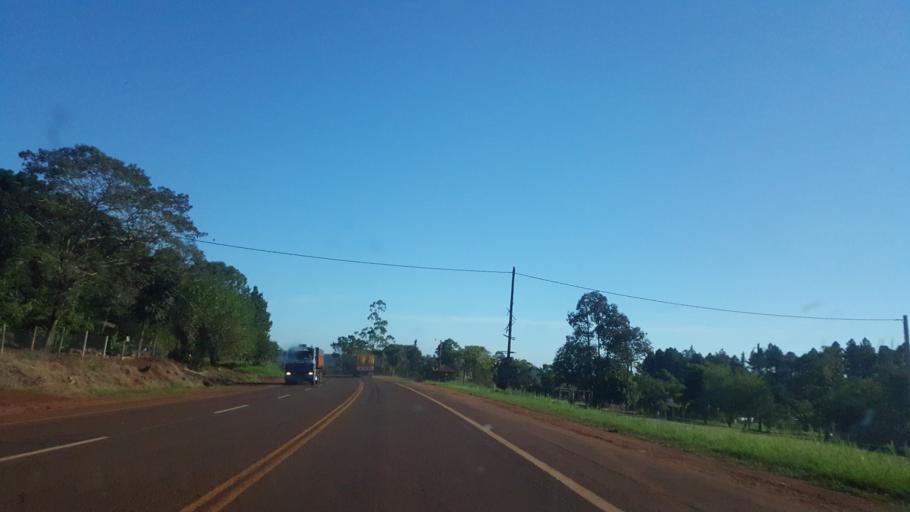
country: AR
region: Misiones
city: Puerto Esperanza
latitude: -26.1789
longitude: -54.5892
